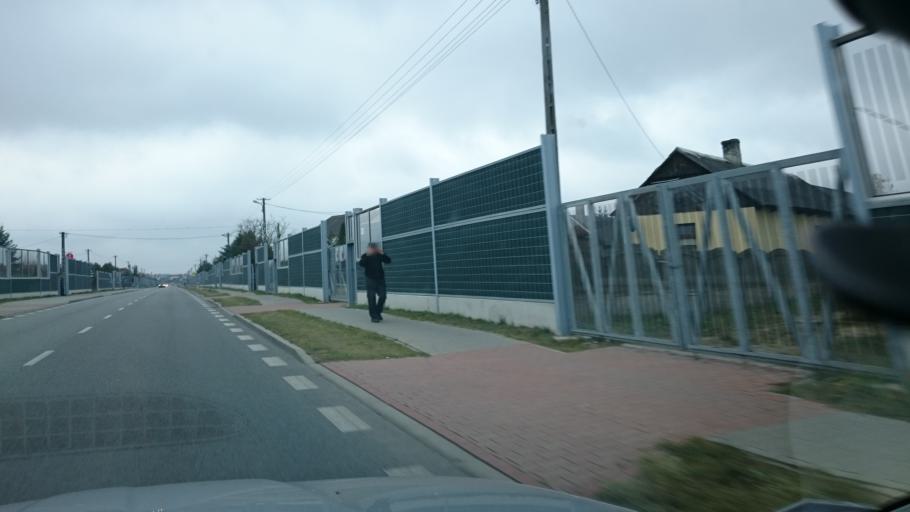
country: PL
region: Swietokrzyskie
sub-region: Powiat konecki
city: Konskie
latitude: 51.1635
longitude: 20.3734
